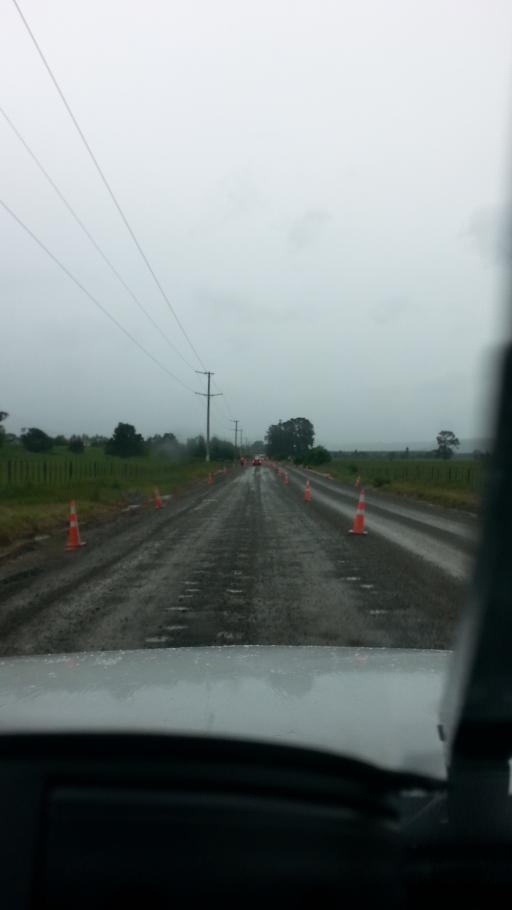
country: NZ
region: Wellington
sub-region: Masterton District
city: Masterton
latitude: -40.8318
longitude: 175.6275
